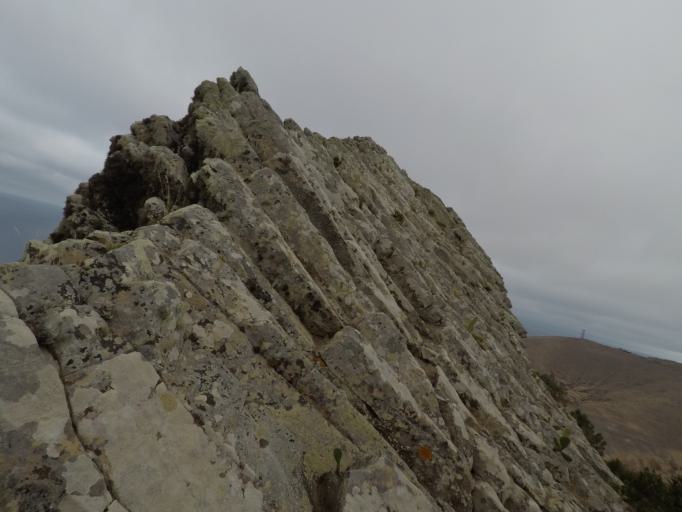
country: PT
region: Madeira
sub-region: Porto Santo
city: Vila de Porto Santo
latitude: 33.0445
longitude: -16.3695
